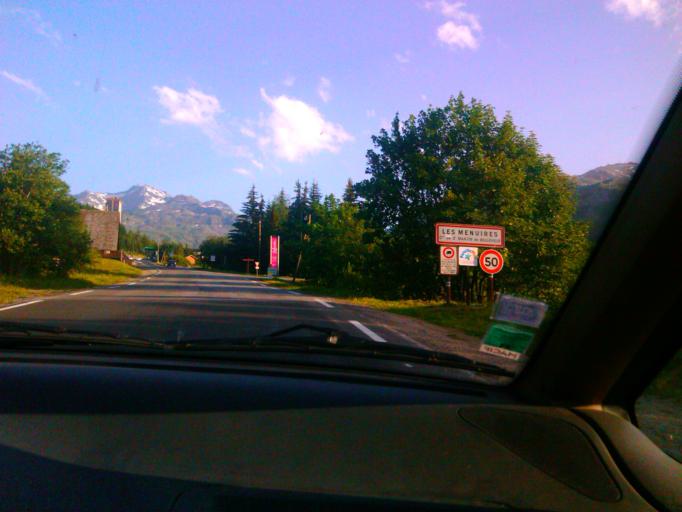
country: FR
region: Rhone-Alpes
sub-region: Departement de la Savoie
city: Saint-Martin-de-Belleville
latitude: 45.3346
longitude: 6.5357
